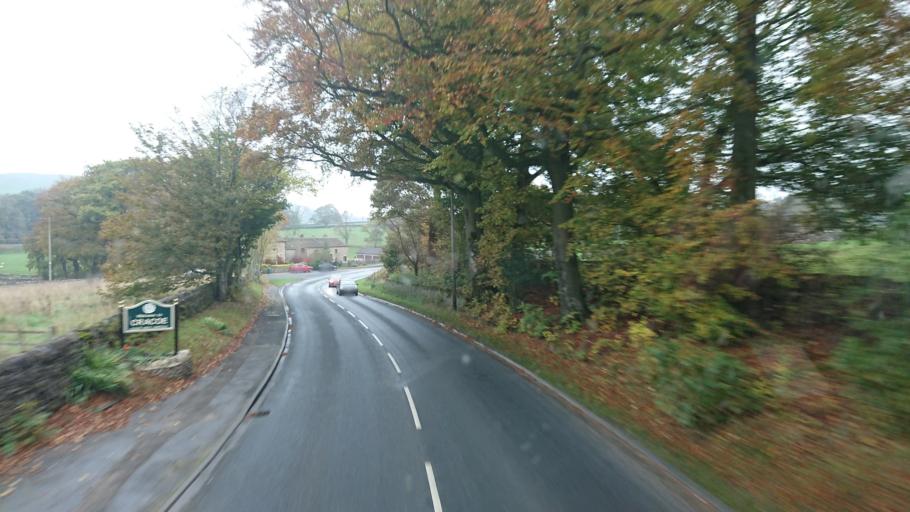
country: GB
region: England
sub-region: North Yorkshire
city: Embsay
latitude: 54.0340
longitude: -2.0417
